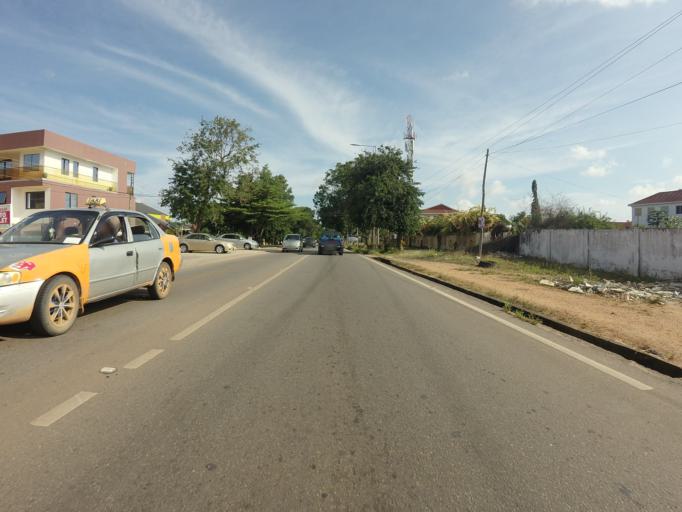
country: GH
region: Greater Accra
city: Medina Estates
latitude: 5.6353
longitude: -0.1613
